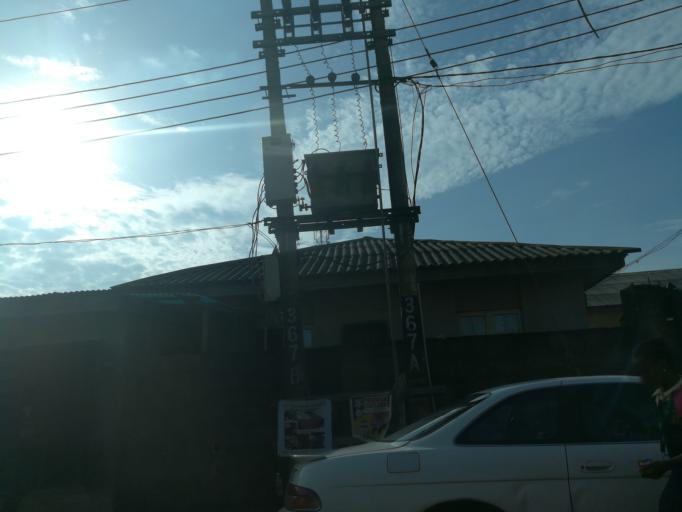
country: NG
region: Lagos
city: Ojota
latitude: 6.6043
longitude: 3.4198
